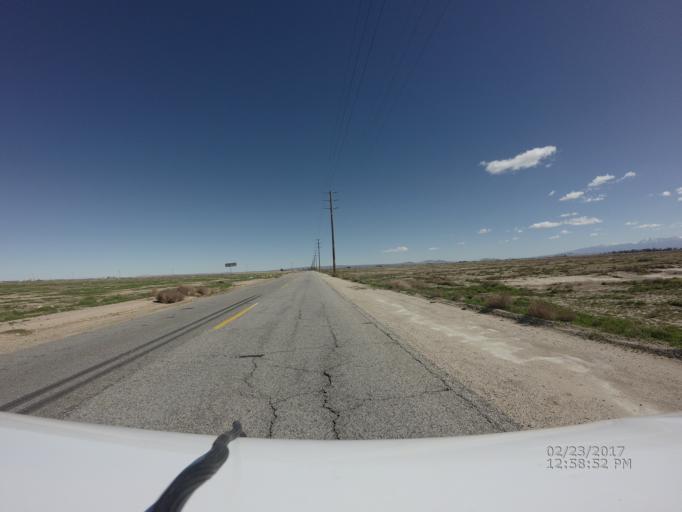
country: US
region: California
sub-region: Los Angeles County
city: Lancaster
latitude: 34.7629
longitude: -118.0399
